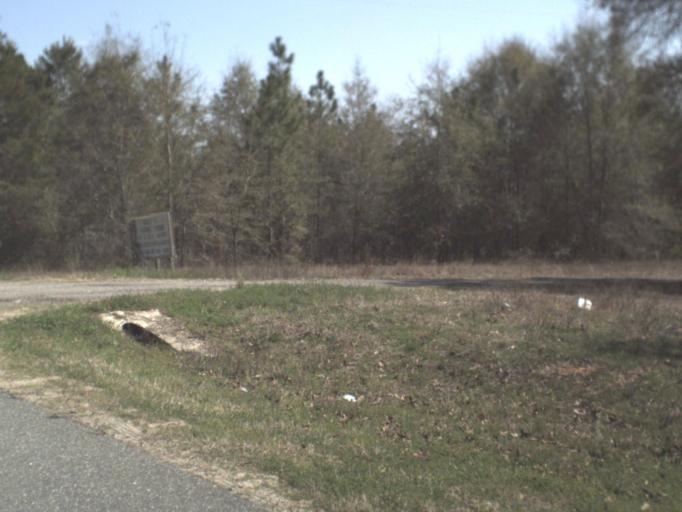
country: US
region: Florida
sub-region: Gadsden County
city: Gretna
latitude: 30.5254
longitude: -84.7989
